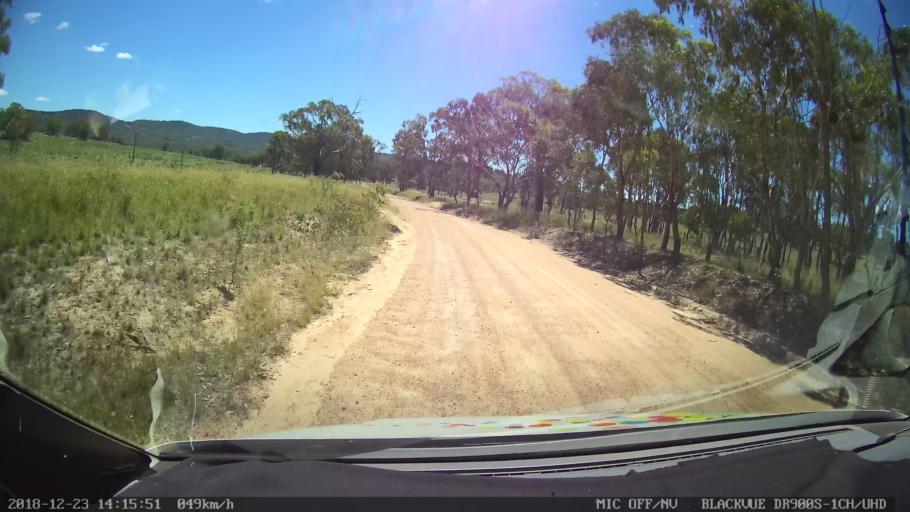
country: AU
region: New South Wales
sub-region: Tamworth Municipality
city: Manilla
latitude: -30.6606
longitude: 151.0232
